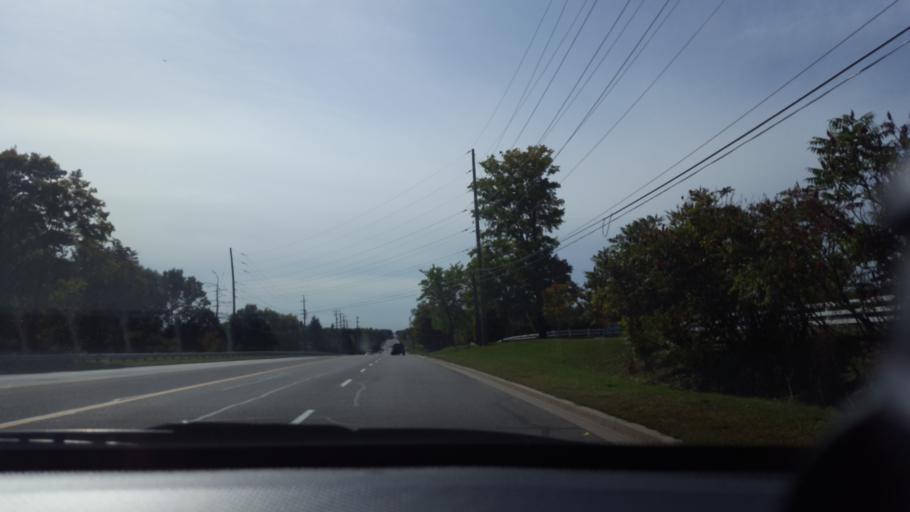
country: CA
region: Ontario
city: Newmarket
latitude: 44.0017
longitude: -79.4961
